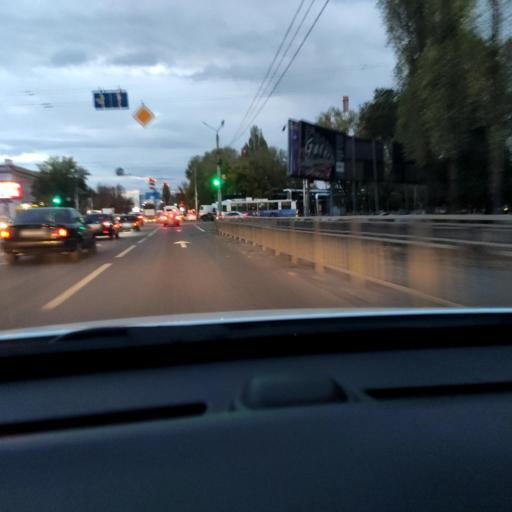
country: RU
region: Voronezj
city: Voronezh
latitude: 51.6313
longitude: 39.2313
